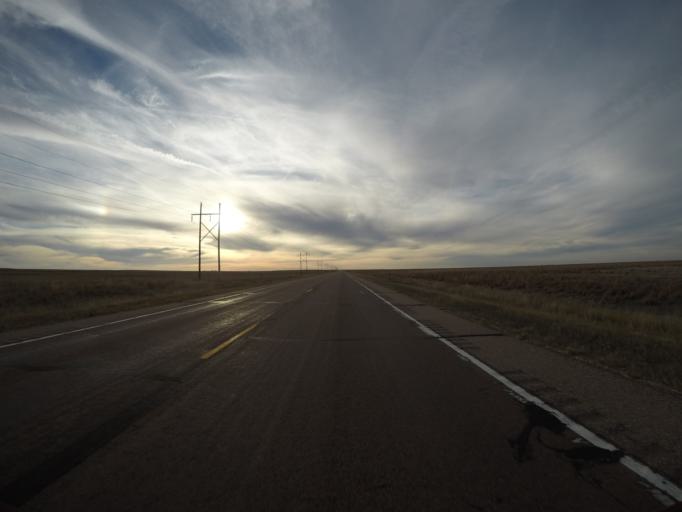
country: US
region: Colorado
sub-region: Yuma County
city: Yuma
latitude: 39.6553
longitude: -102.7750
